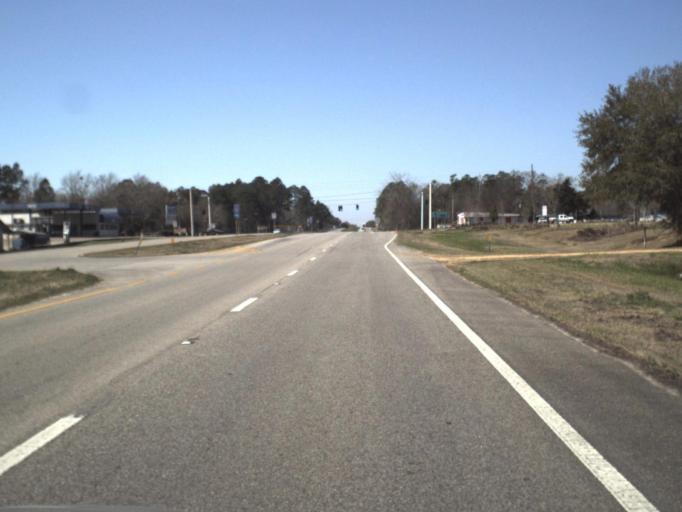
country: US
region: Florida
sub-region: Jackson County
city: Sneads
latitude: 30.7193
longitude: -85.0176
